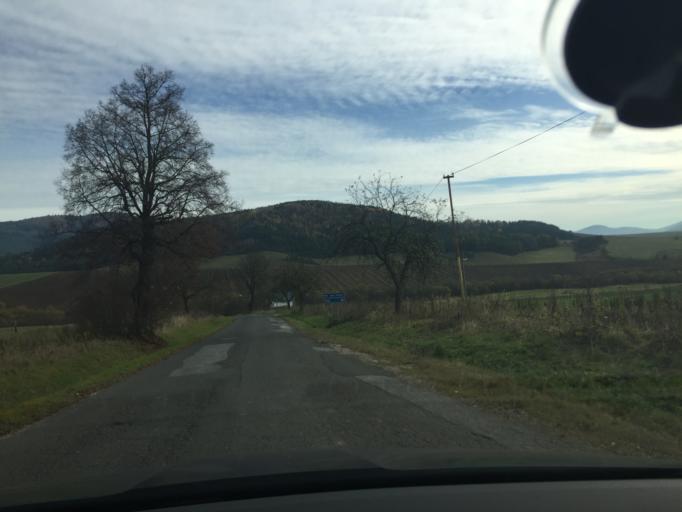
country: SK
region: Presovsky
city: Spisske Podhradie
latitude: 48.9880
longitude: 20.7915
